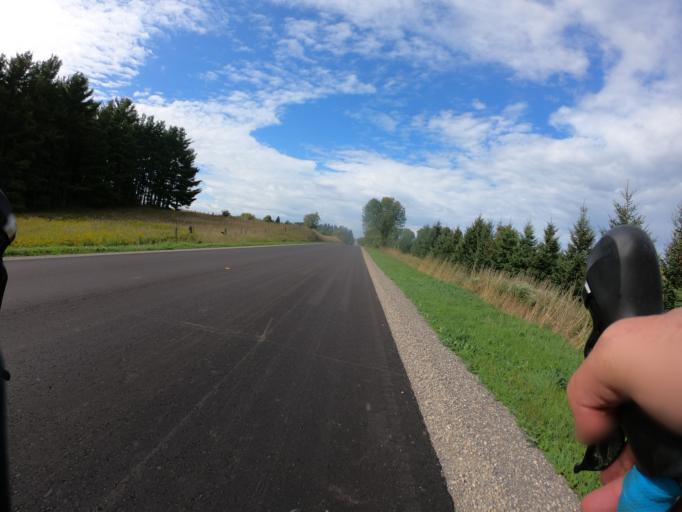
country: CA
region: Ontario
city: Kitchener
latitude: 43.3811
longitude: -80.6224
